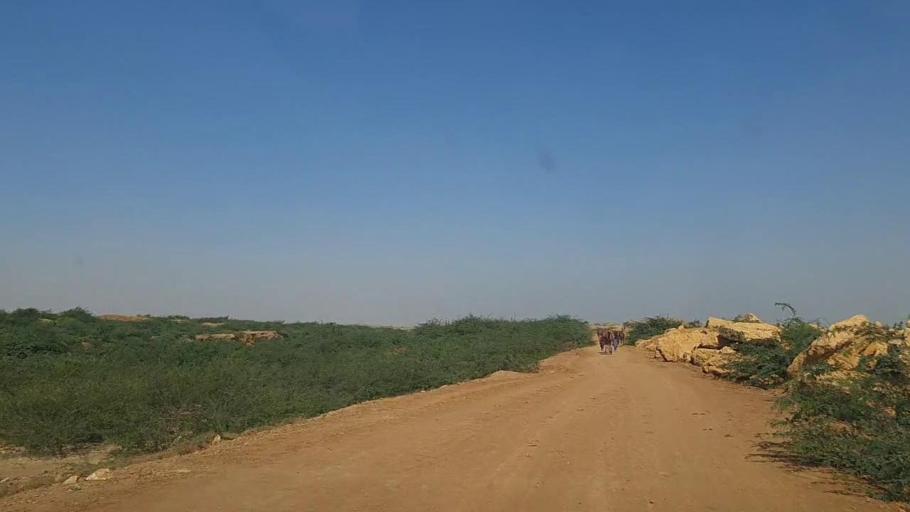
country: PK
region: Sindh
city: Thatta
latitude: 24.8316
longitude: 68.0190
